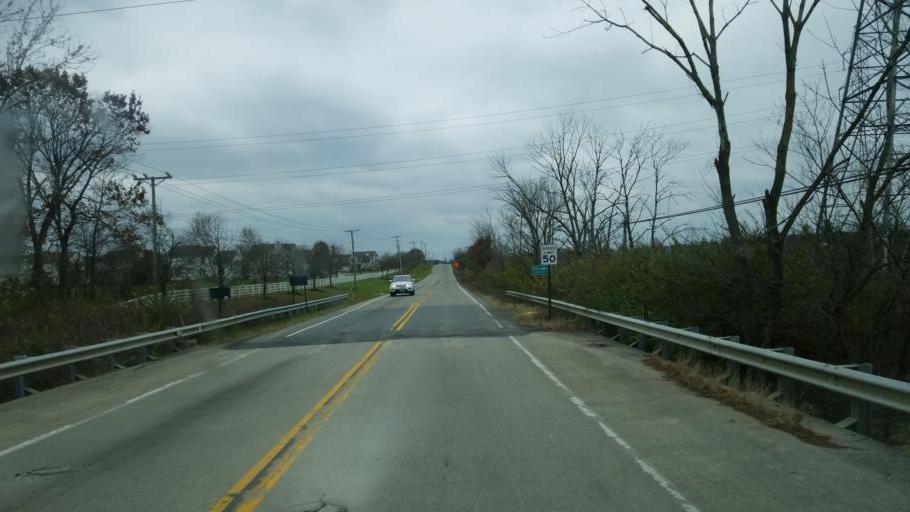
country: US
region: Ohio
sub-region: Franklin County
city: New Albany
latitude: 40.0793
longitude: -82.8434
